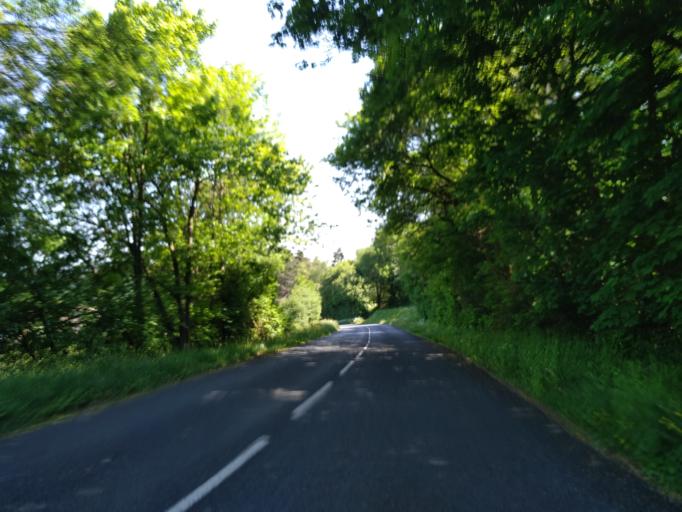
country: FR
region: Rhone-Alpes
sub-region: Departement du Rhone
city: Limonest
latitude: 45.8320
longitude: 4.8045
